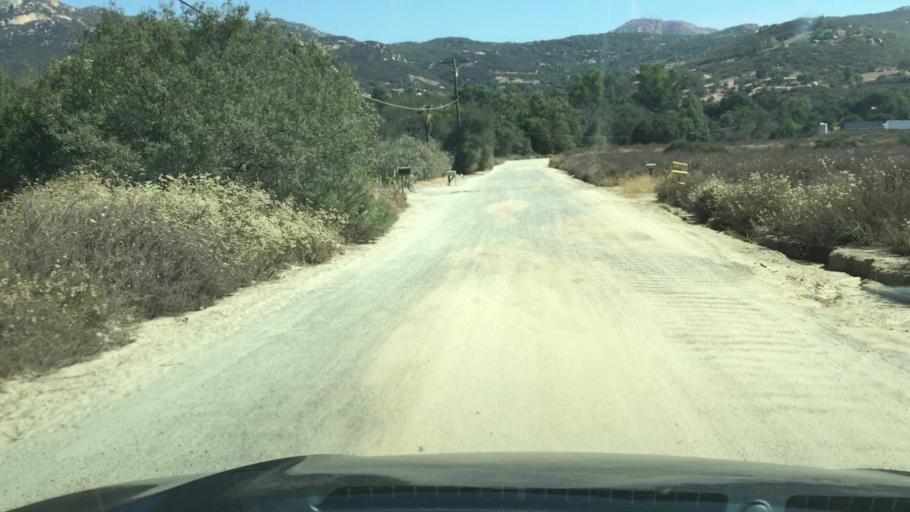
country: US
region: California
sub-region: San Diego County
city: Alpine
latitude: 32.7548
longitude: -116.7571
